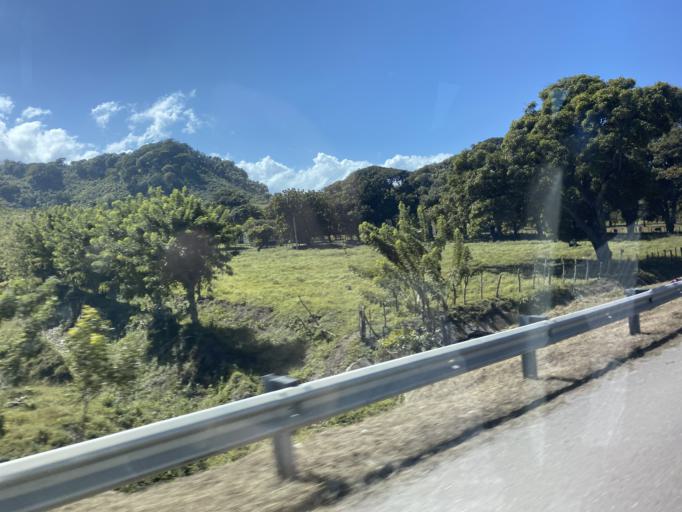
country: DO
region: Puerto Plata
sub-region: Puerto Plata
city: Puerto Plata
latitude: 19.8298
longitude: -70.7630
